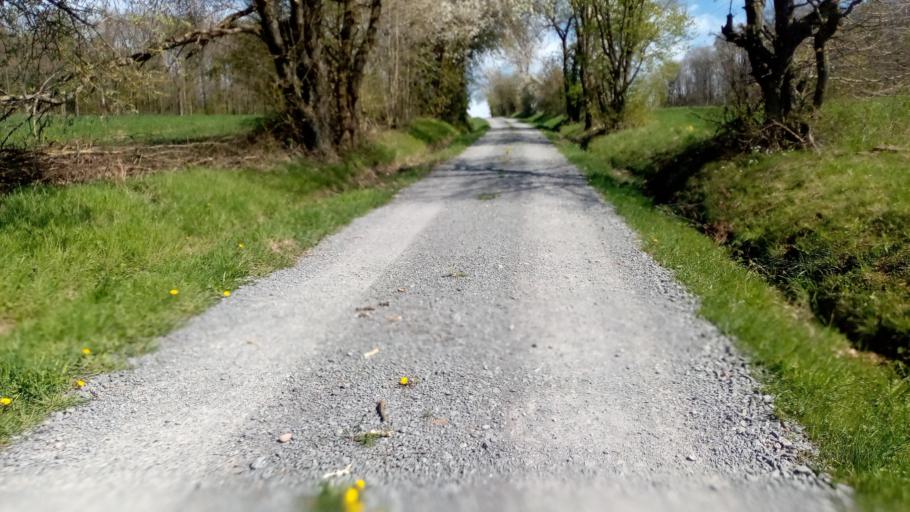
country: DE
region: Bavaria
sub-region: Regierungsbezirk Unterfranken
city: Hasloch
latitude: 49.7968
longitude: 9.5040
